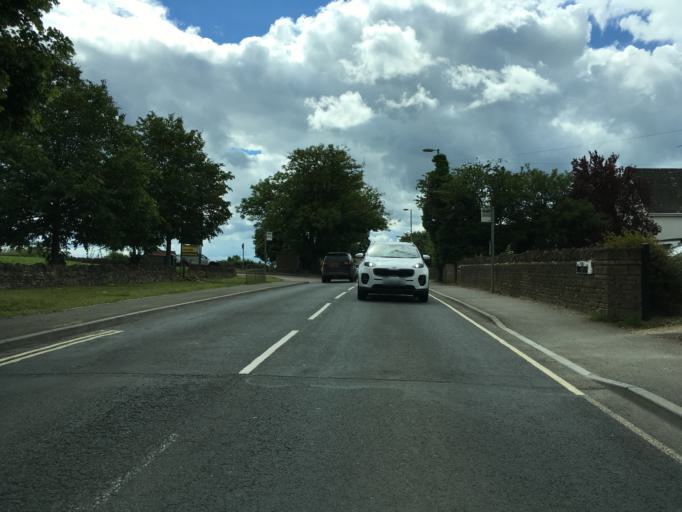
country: GB
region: England
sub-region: Oxfordshire
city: Chipping Norton
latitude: 51.9366
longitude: -1.5438
